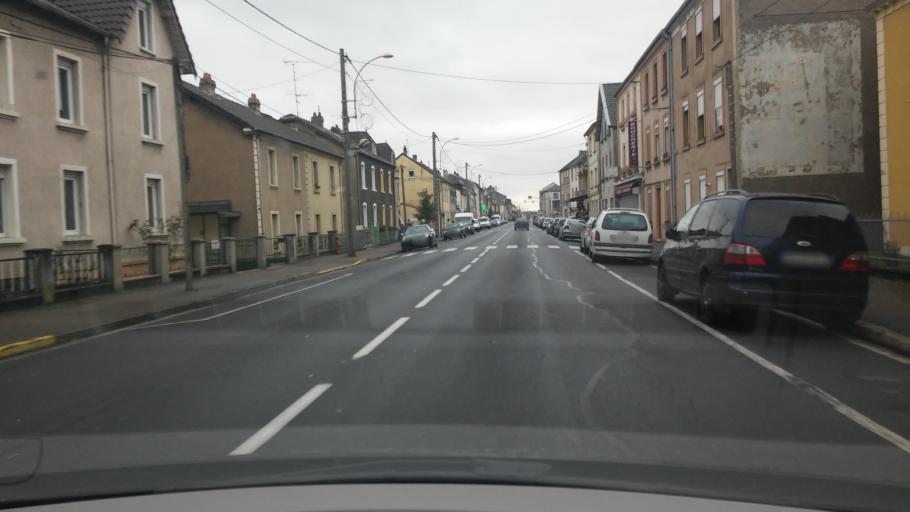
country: FR
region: Lorraine
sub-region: Departement de la Moselle
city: Mondelange
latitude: 49.2589
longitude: 6.1699
